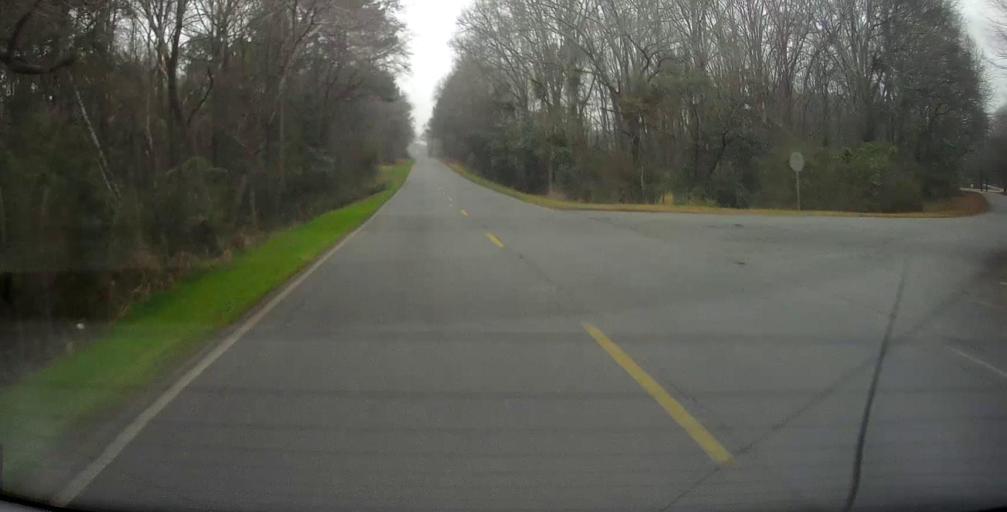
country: US
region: Georgia
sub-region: Spalding County
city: East Griffin
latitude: 33.2317
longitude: -84.2427
